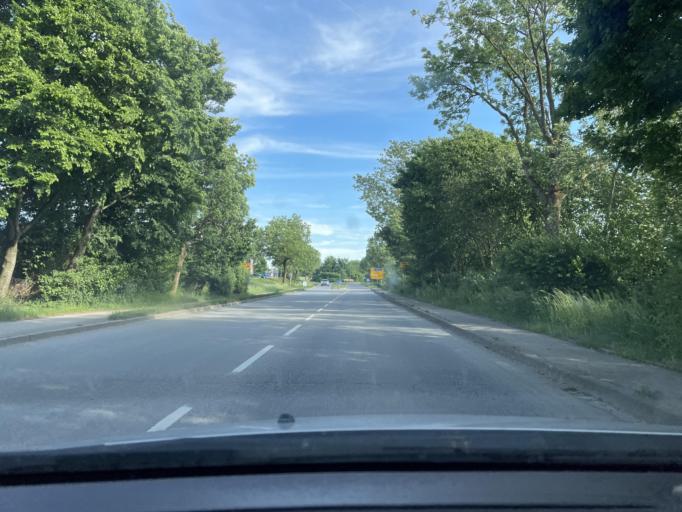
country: DE
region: Bavaria
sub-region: Lower Bavaria
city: Weihmichl
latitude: 48.5851
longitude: 12.0634
